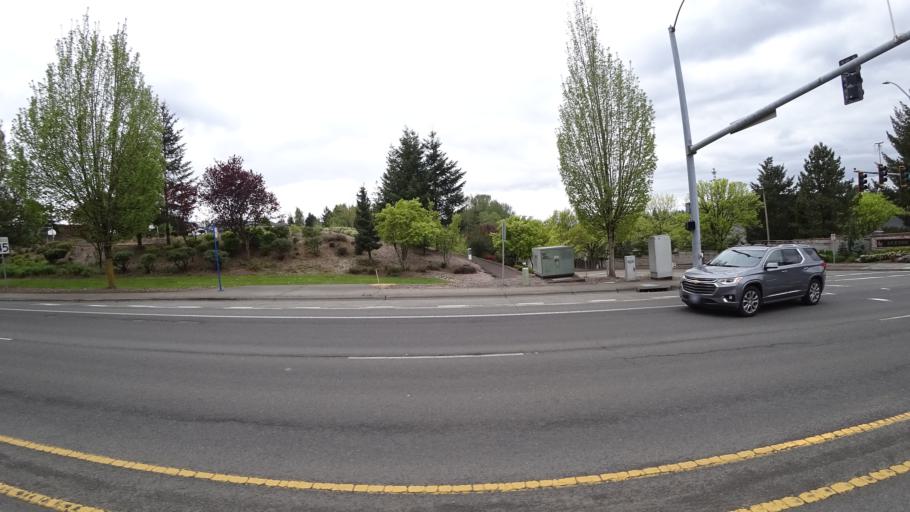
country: US
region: Oregon
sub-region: Washington County
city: Beaverton
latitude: 45.4599
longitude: -122.8261
